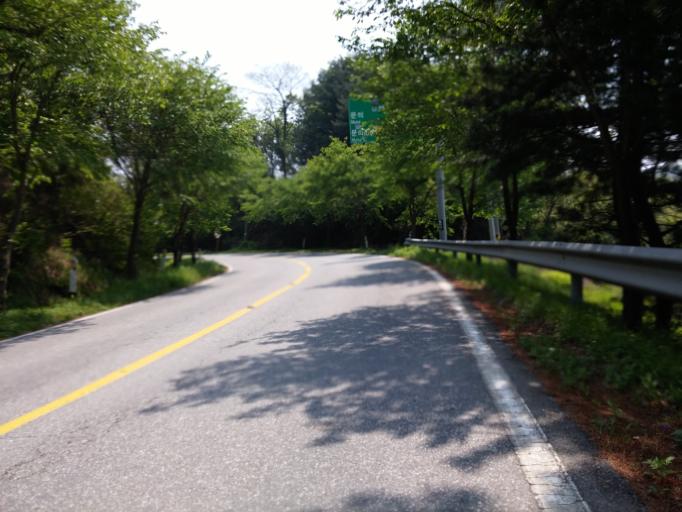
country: KR
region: Chungcheongbuk-do
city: Okcheon
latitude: 36.4398
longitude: 127.5716
